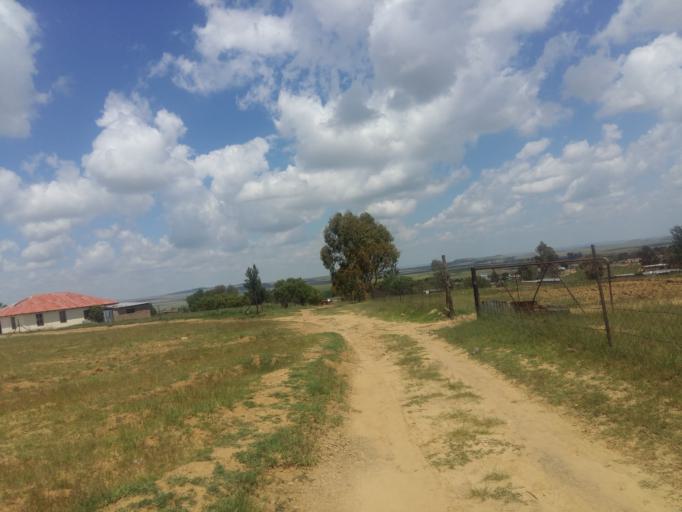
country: LS
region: Mafeteng
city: Mafeteng
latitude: -29.7550
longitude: 27.1154
